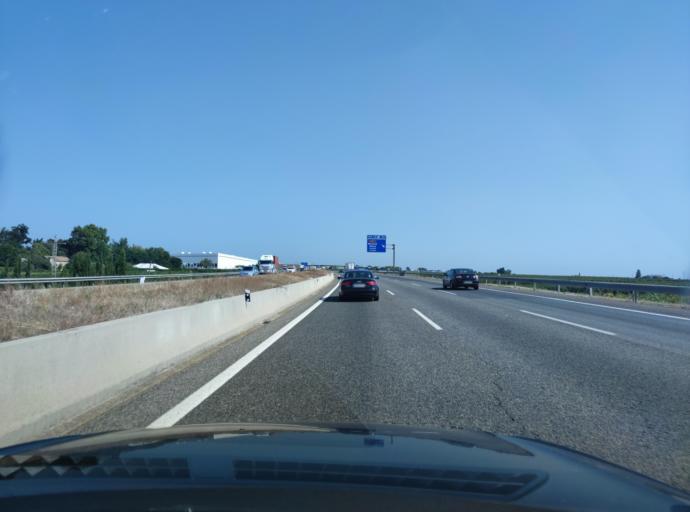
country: ES
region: Valencia
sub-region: Provincia de Valencia
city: Alginet
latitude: 39.2681
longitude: -0.4585
